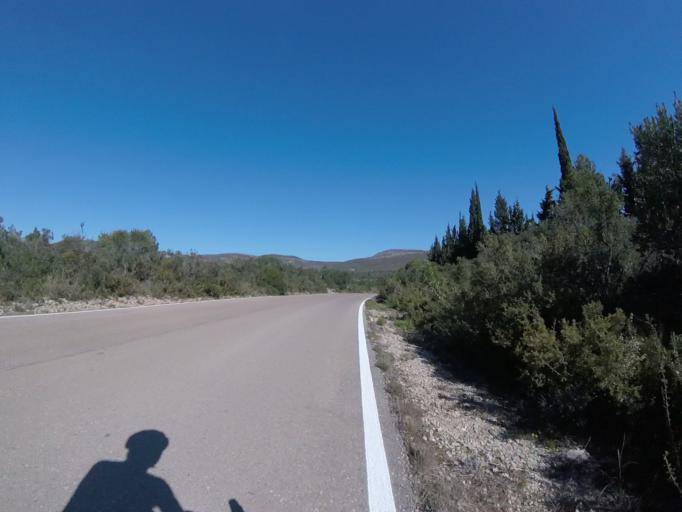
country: ES
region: Valencia
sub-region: Provincia de Castello
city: Santa Magdalena de Pulpis
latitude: 40.3698
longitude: 0.2744
